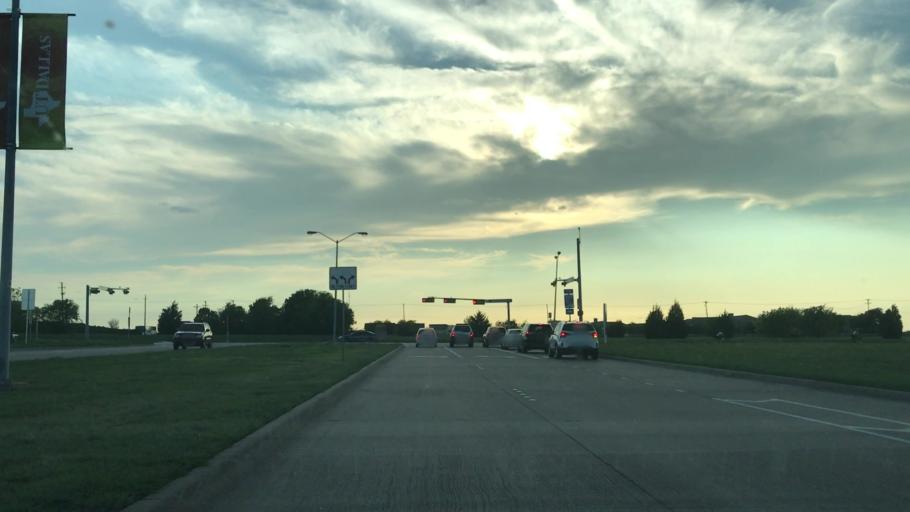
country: US
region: Texas
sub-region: Dallas County
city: Richardson
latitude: 32.9931
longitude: -96.7553
